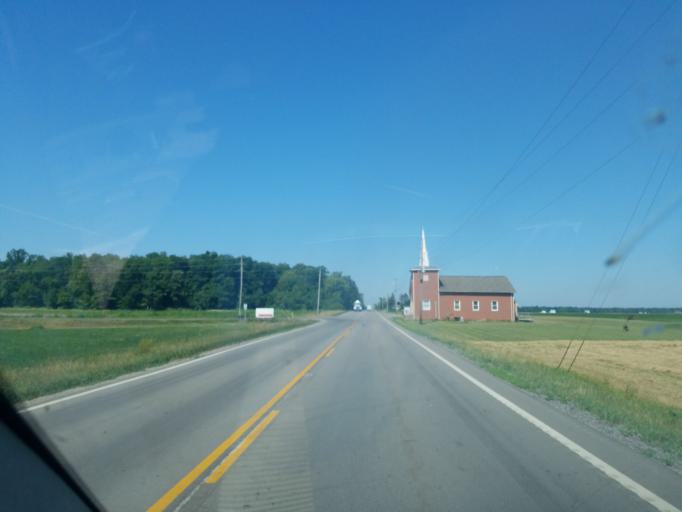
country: US
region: Ohio
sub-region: Logan County
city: Lakeview
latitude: 40.4393
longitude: -83.9451
